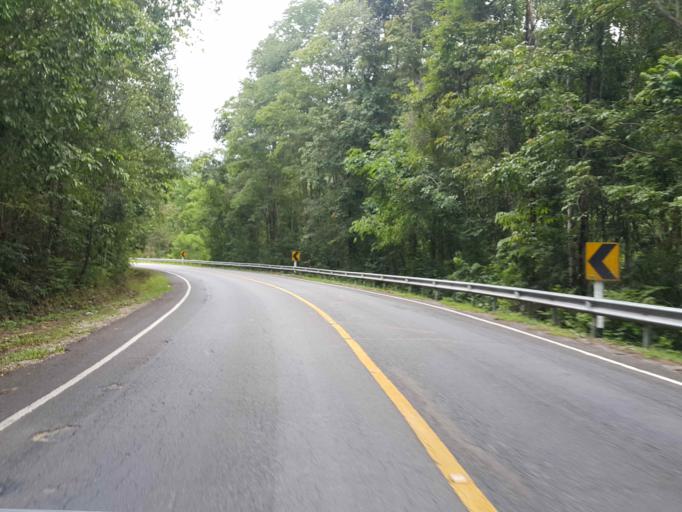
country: TH
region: Chiang Mai
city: Chom Thong
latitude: 18.5283
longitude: 98.6191
